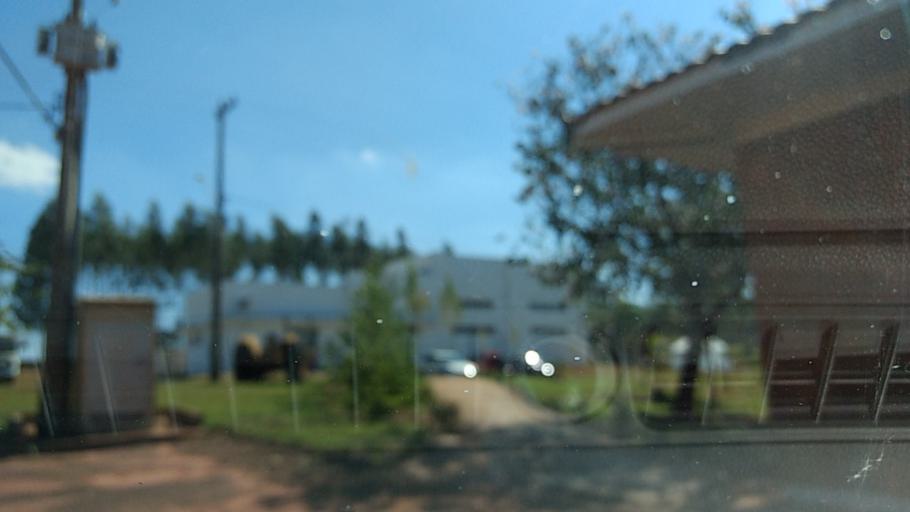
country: BR
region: Sao Paulo
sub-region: Botucatu
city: Botucatu
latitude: -22.8487
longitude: -48.4349
